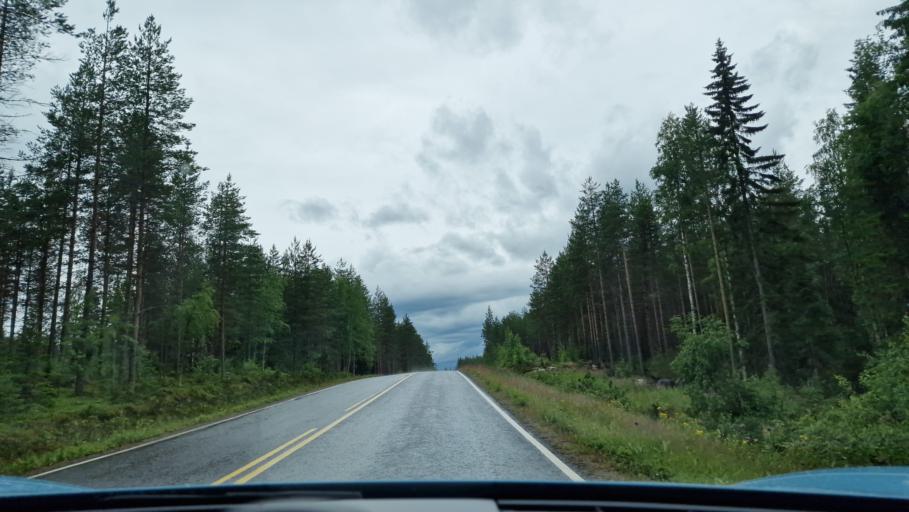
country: FI
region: Central Finland
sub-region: Saarijaervi-Viitasaari
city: Pylkoenmaeki
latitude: 62.6689
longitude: 24.5293
